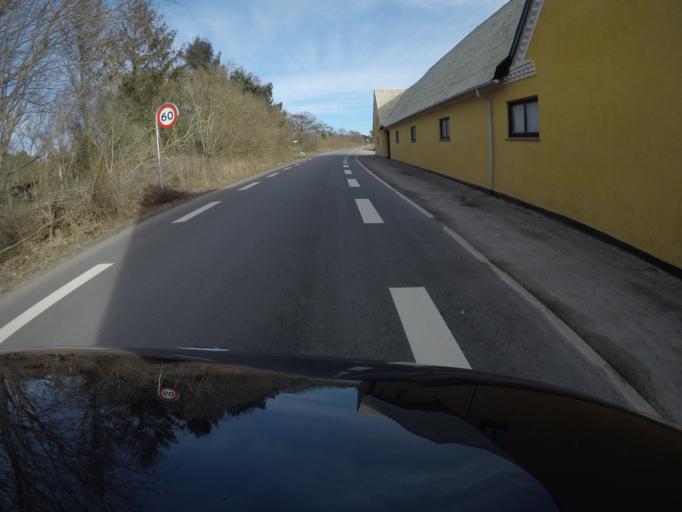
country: DK
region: Capital Region
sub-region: Halsnaes Kommune
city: Liseleje
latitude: 55.9934
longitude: 11.9194
